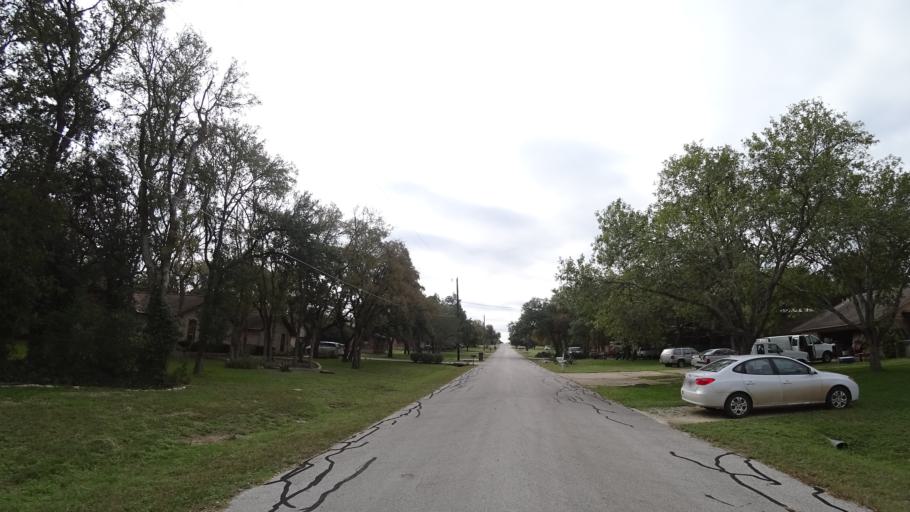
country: US
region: Texas
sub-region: Travis County
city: Shady Hollow
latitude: 30.1379
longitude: -97.8886
